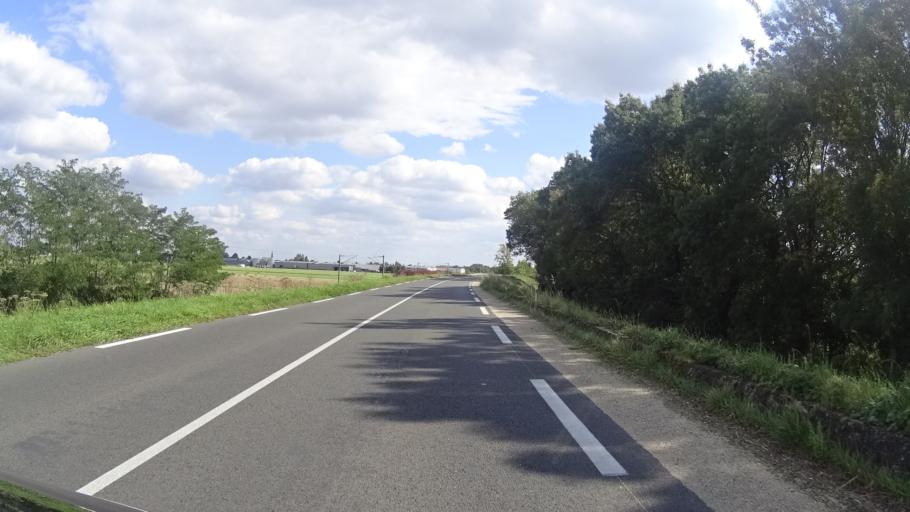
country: FR
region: Pays de la Loire
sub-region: Departement de Maine-et-Loire
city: La Menitre
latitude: 47.4048
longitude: -0.2887
